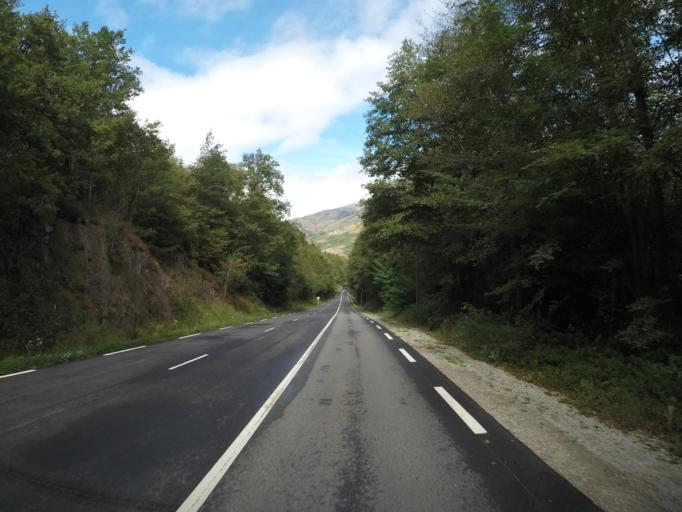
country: FR
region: Midi-Pyrenees
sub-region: Departement de l'Ariege
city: Ax-les-Thermes
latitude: 42.7518
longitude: 1.7719
